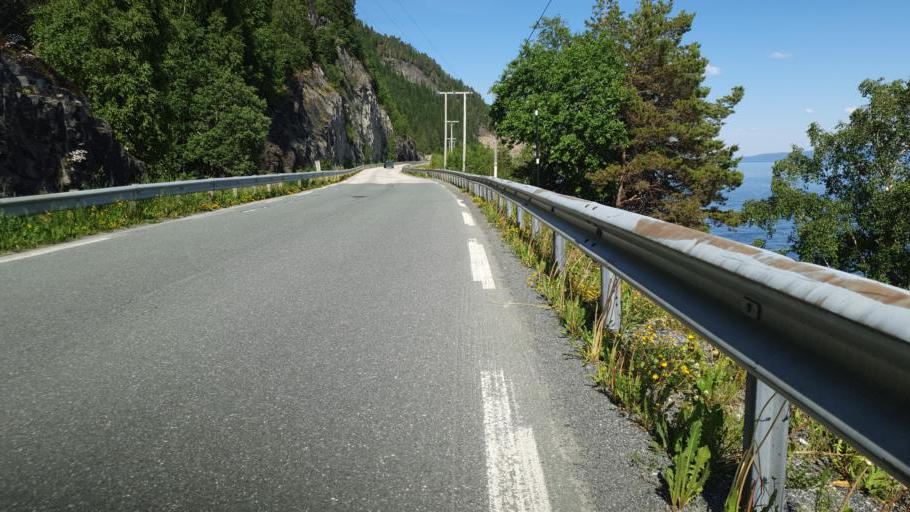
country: NO
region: Nord-Trondelag
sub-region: Leksvik
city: Leksvik
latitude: 63.6050
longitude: 10.4875
